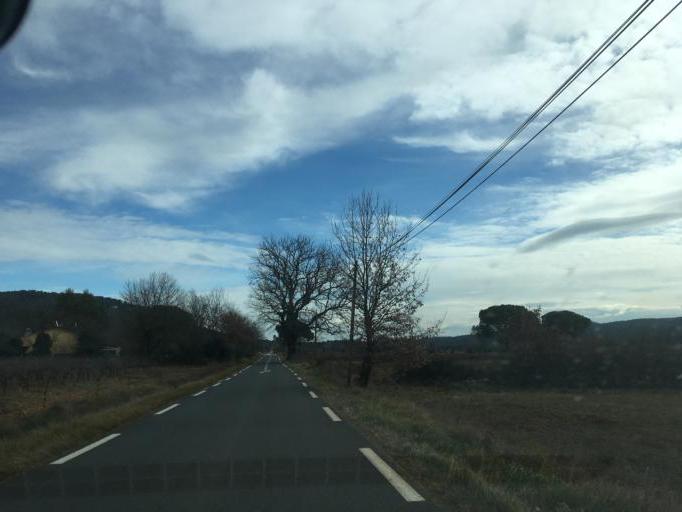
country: FR
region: Provence-Alpes-Cote d'Azur
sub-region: Departement du Var
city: Bras
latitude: 43.4471
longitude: 5.9985
